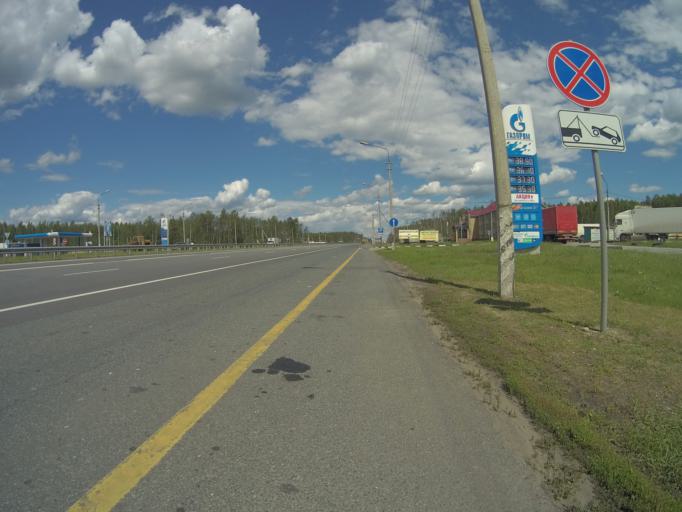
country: RU
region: Vladimir
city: Sudogda
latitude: 56.1323
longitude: 40.8817
